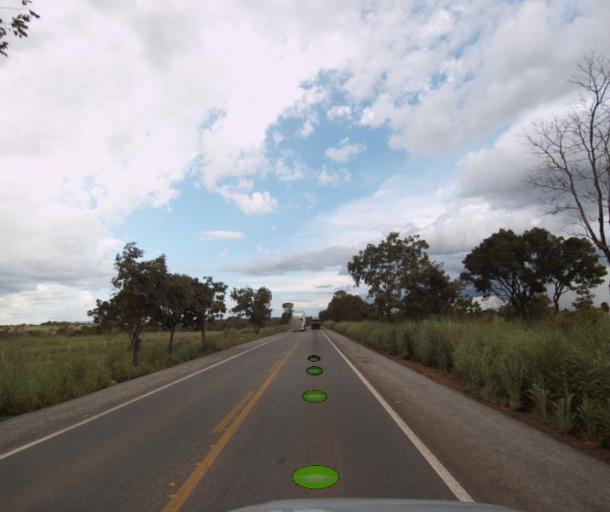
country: BR
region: Goias
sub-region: Porangatu
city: Porangatu
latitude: -13.3593
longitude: -49.1242
